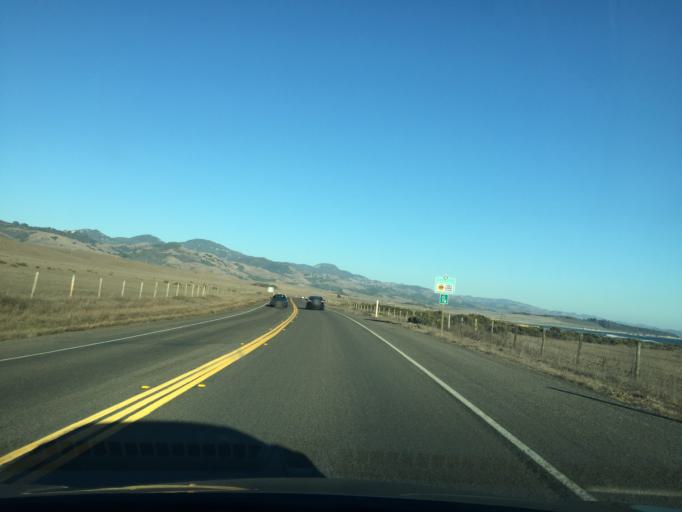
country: US
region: California
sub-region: San Luis Obispo County
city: Cambria
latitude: 35.6536
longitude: -121.2407
